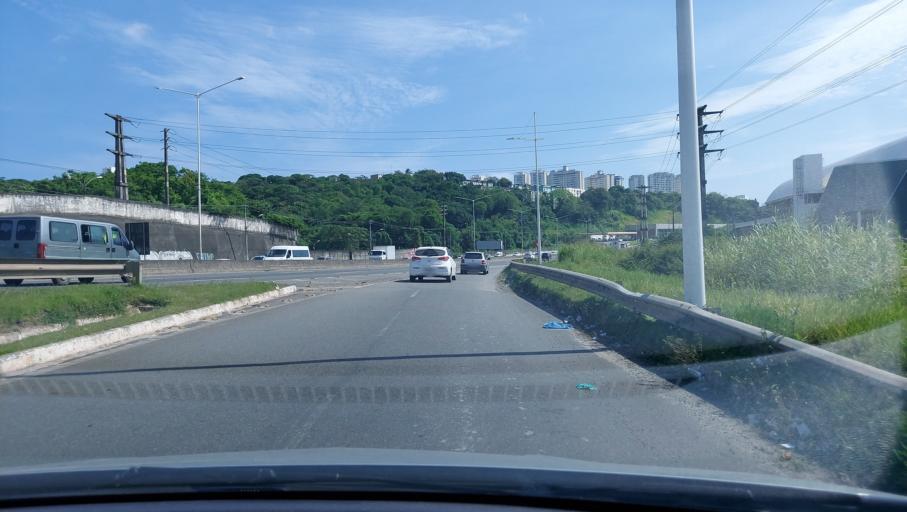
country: BR
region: Bahia
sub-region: Salvador
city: Salvador
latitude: -12.9554
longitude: -38.4716
